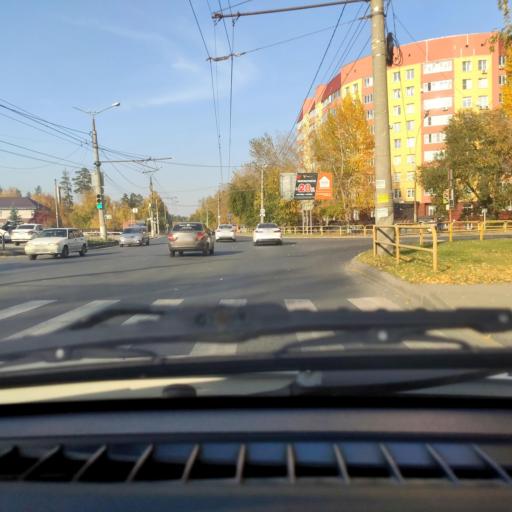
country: RU
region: Samara
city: Tol'yatti
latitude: 53.5009
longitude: 49.3899
